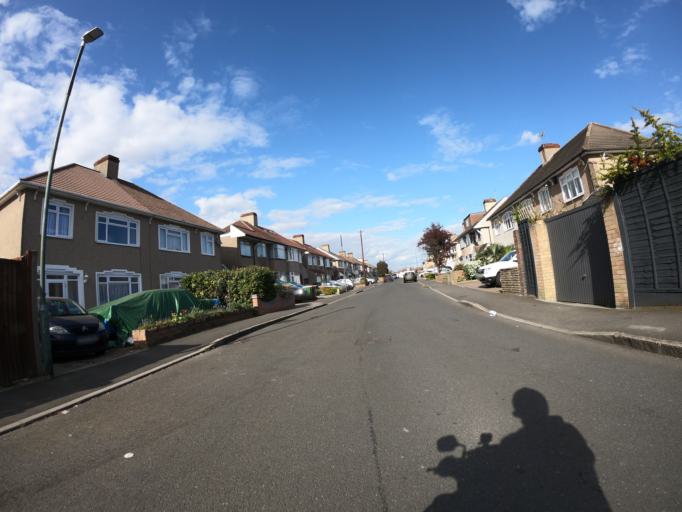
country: GB
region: England
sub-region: Greater London
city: Bexleyheath
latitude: 51.4728
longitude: 0.1327
